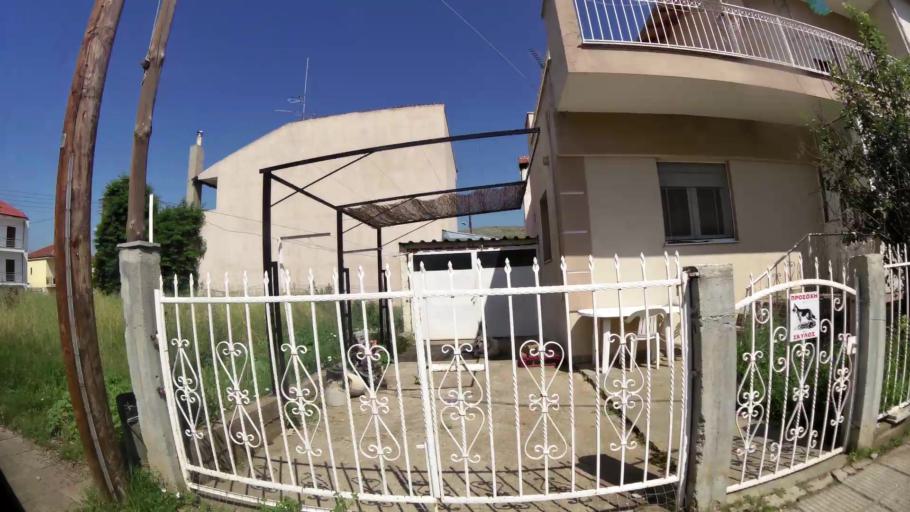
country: GR
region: West Macedonia
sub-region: Nomos Kozanis
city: Koila
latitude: 40.3389
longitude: 21.7869
